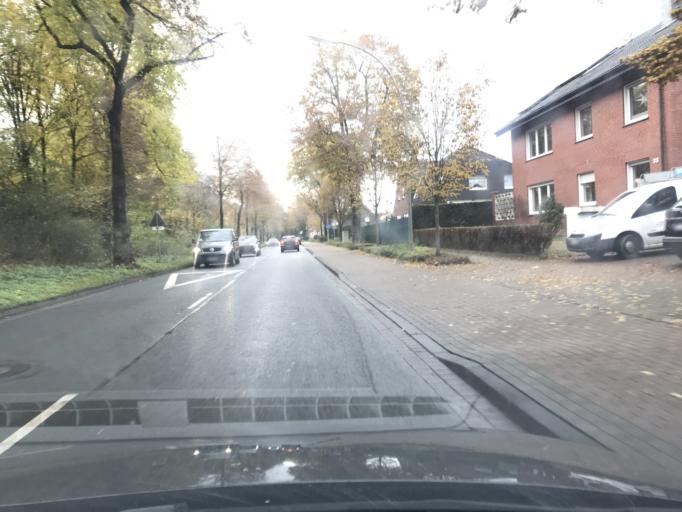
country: DE
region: North Rhine-Westphalia
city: Oelde
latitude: 51.8328
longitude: 8.1621
